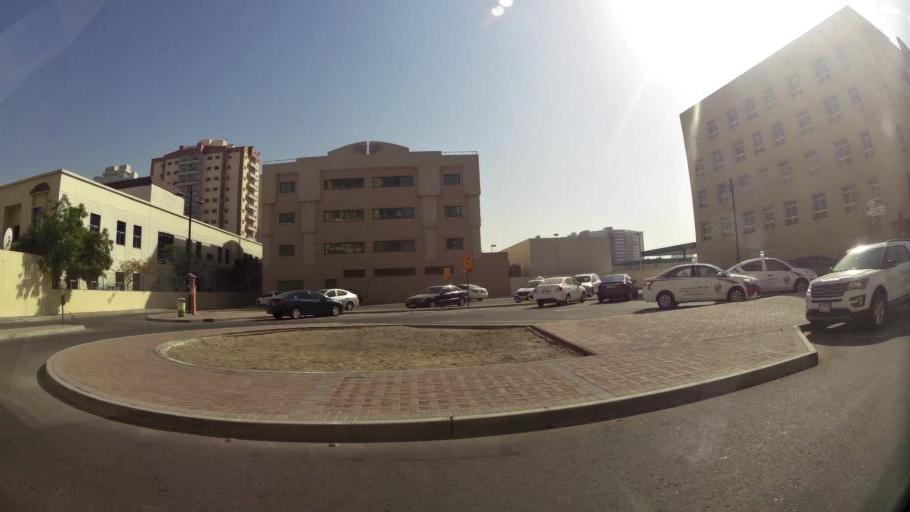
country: AE
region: Ash Shariqah
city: Sharjah
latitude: 25.2946
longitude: 55.3748
